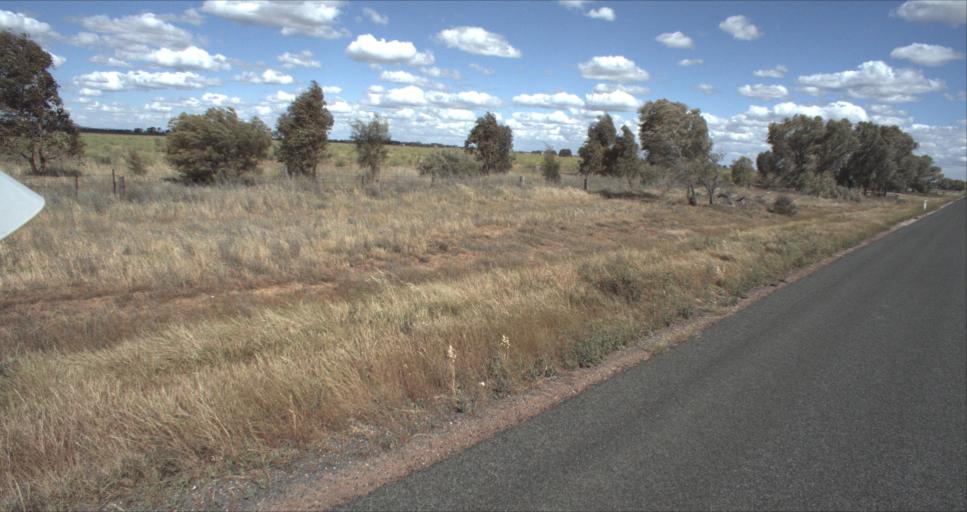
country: AU
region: New South Wales
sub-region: Leeton
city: Leeton
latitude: -34.4364
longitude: 146.2572
